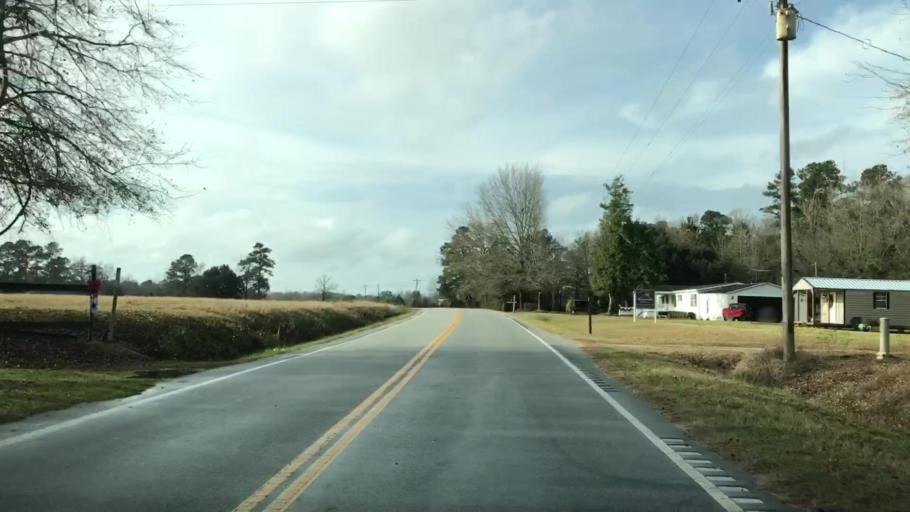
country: US
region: South Carolina
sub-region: Williamsburg County
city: Andrews
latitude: 33.5010
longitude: -79.5166
